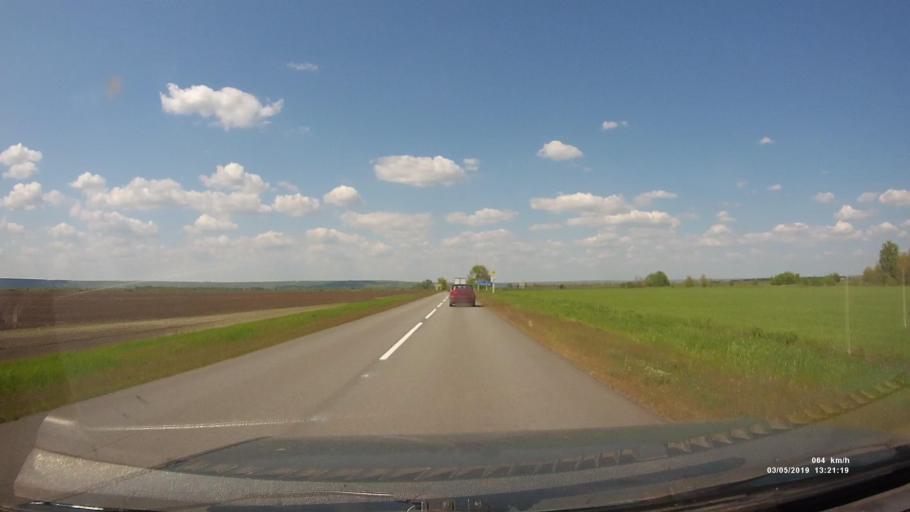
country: RU
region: Rostov
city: Semikarakorsk
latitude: 47.5539
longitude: 40.7478
